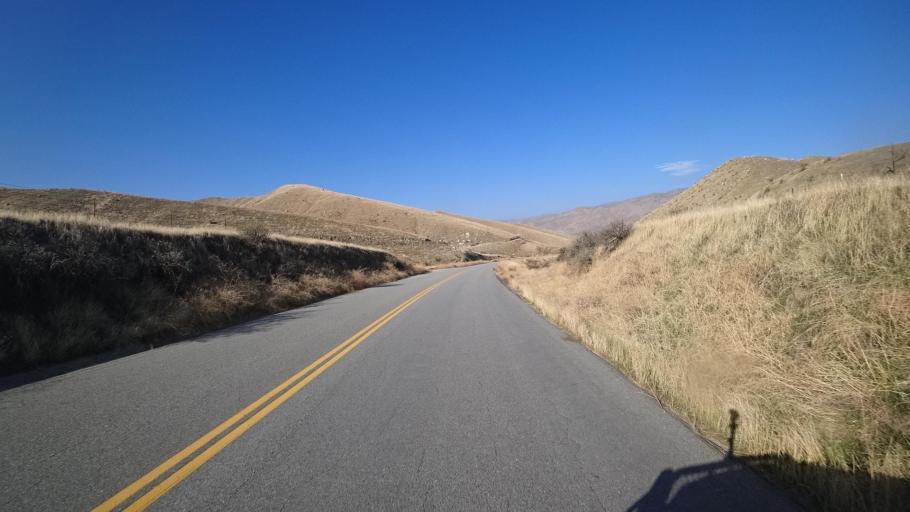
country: US
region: California
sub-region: Kern County
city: Bear Valley Springs
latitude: 35.2924
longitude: -118.6962
